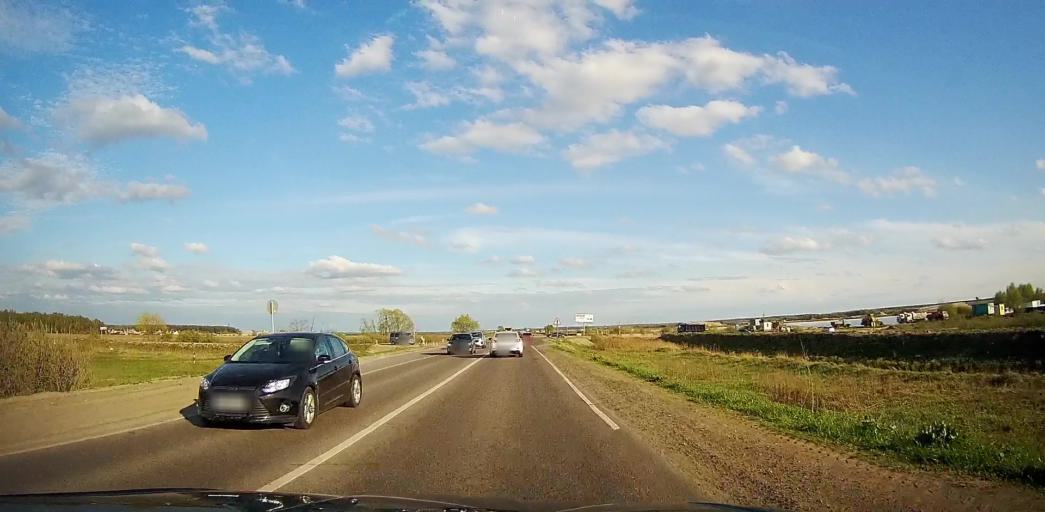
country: RU
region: Moskovskaya
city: Ramenskoye
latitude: 55.5129
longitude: 38.2782
